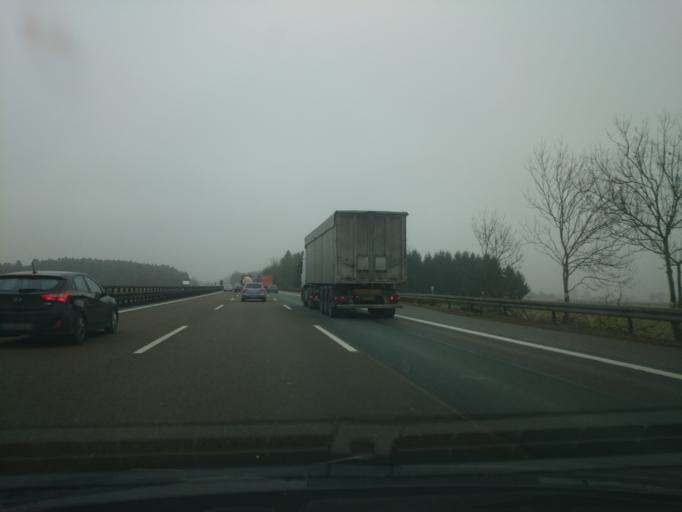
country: DE
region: Bavaria
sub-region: Upper Bavaria
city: Manching
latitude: 48.6948
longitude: 11.4915
